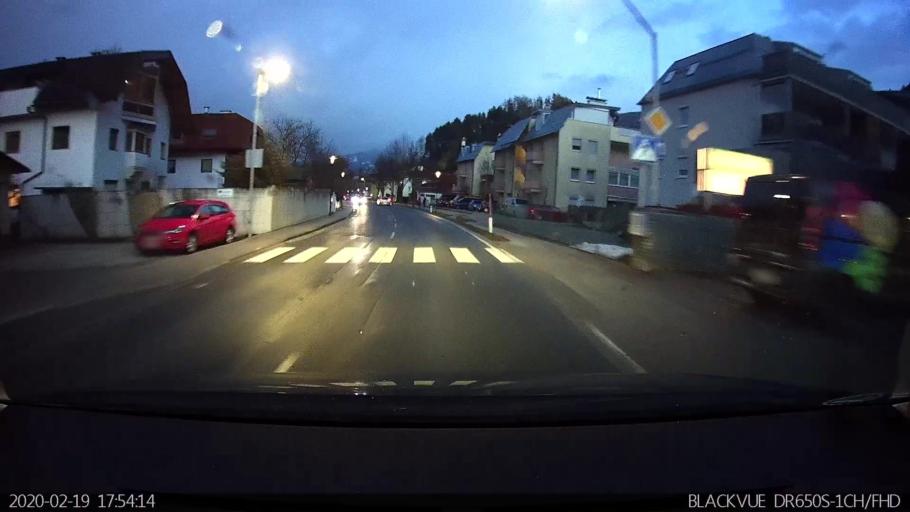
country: AT
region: Tyrol
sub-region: Politischer Bezirk Innsbruck Land
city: Volders
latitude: 47.2878
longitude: 11.5722
